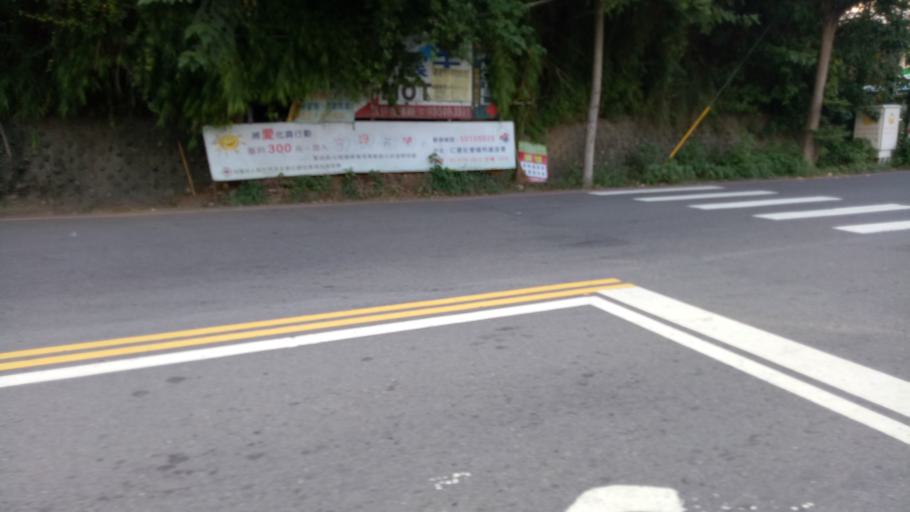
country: TW
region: Taiwan
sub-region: Hsinchu
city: Hsinchu
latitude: 24.7746
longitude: 120.9670
